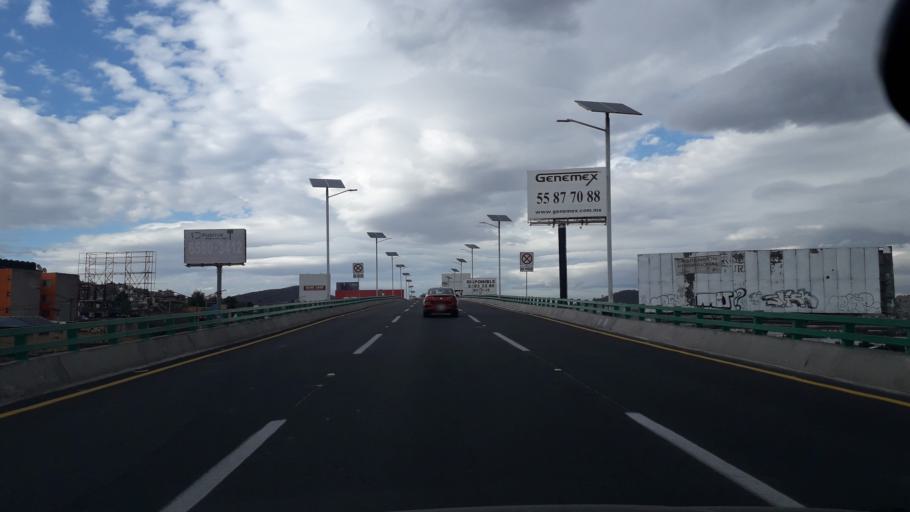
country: MX
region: Mexico
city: Tlalnepantla
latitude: 19.5571
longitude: -99.2061
